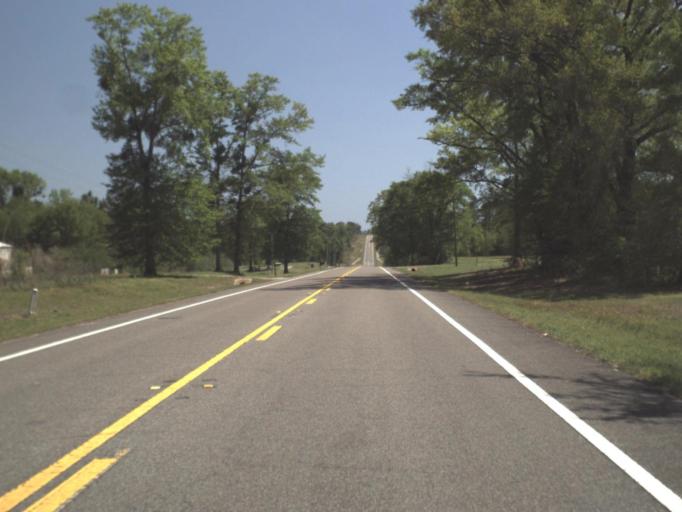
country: US
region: Alabama
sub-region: Escambia County
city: East Brewton
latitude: 30.9255
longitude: -87.0523
